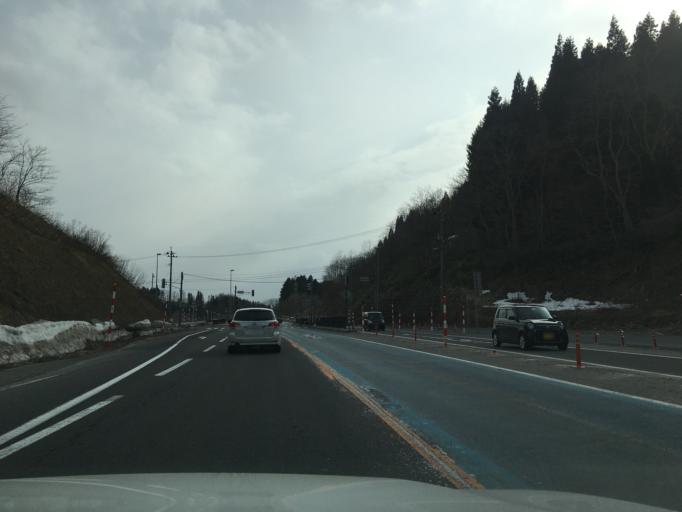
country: JP
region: Aomori
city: Namioka
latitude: 40.7744
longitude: 140.5995
